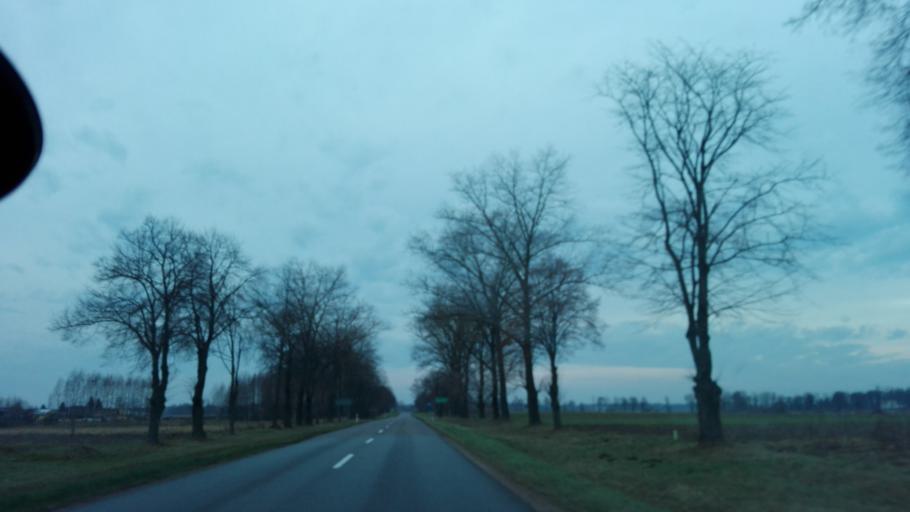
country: PL
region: Lublin Voivodeship
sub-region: Powiat radzynski
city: Wohyn
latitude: 51.7795
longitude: 22.7727
